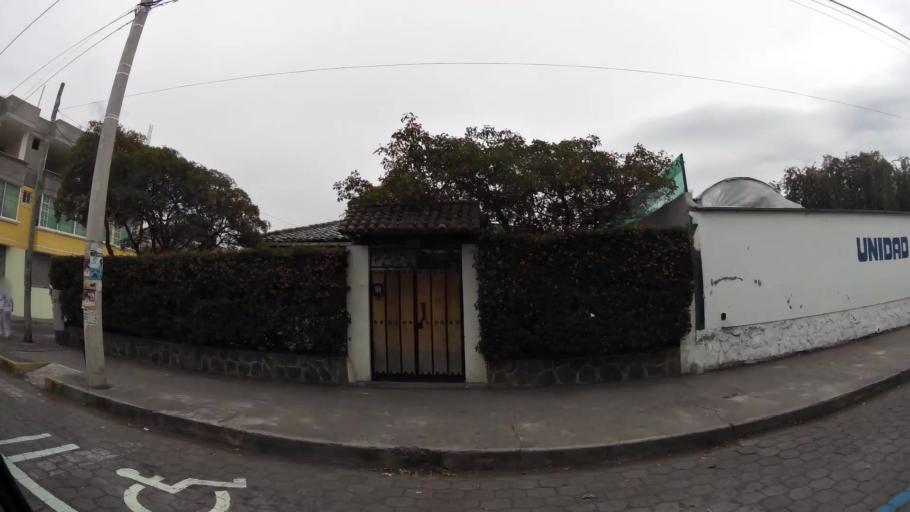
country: EC
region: Cotopaxi
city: Latacunga
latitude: -0.9403
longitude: -78.6131
